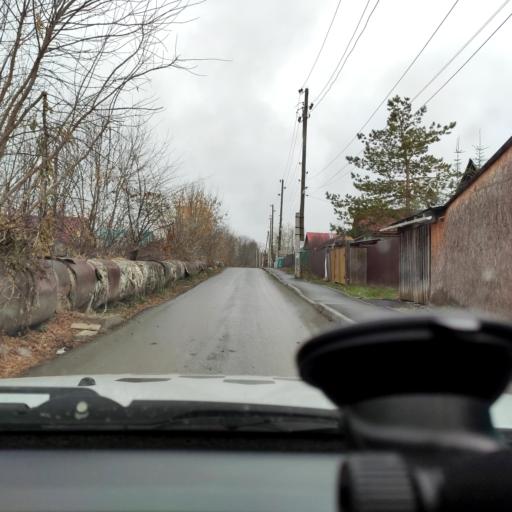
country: RU
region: Perm
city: Kondratovo
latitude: 57.9611
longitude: 56.1499
